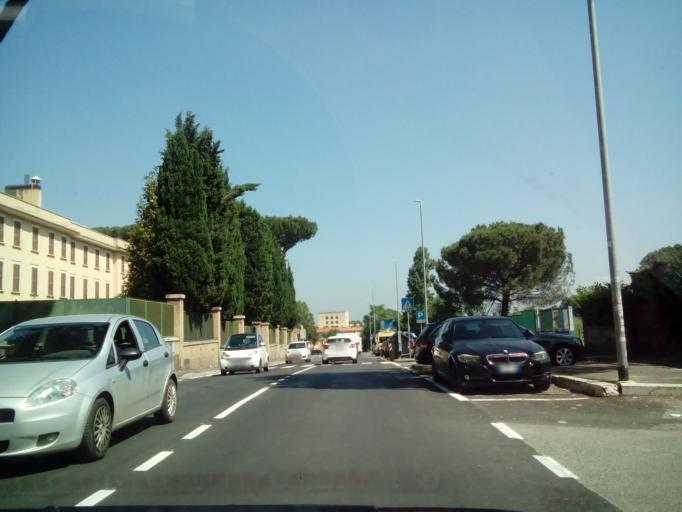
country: IT
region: Latium
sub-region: Citta metropolitana di Roma Capitale
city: Rome
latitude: 41.8870
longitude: 12.5767
